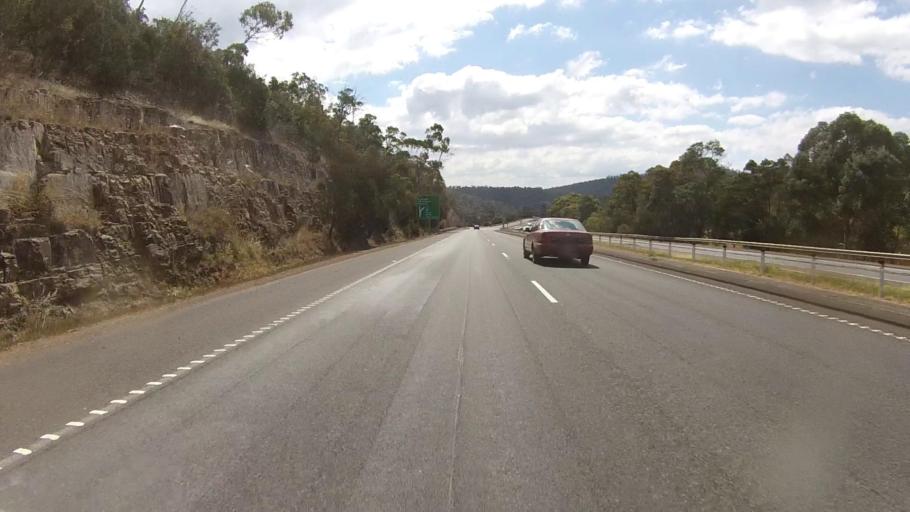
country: AU
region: Tasmania
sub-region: Clarence
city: Cambridge
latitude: -42.8495
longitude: 147.4193
